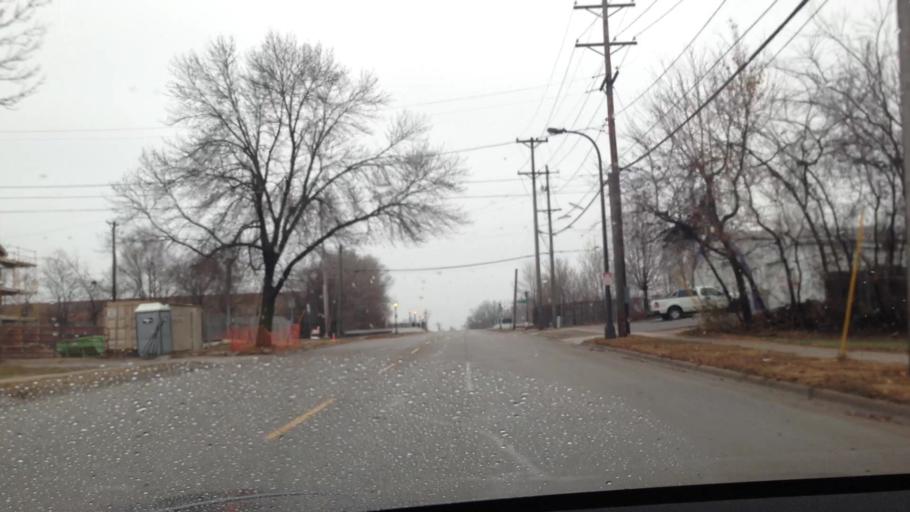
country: US
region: Minnesota
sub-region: Ramsey County
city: Saint Paul
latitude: 44.9675
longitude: -93.0761
